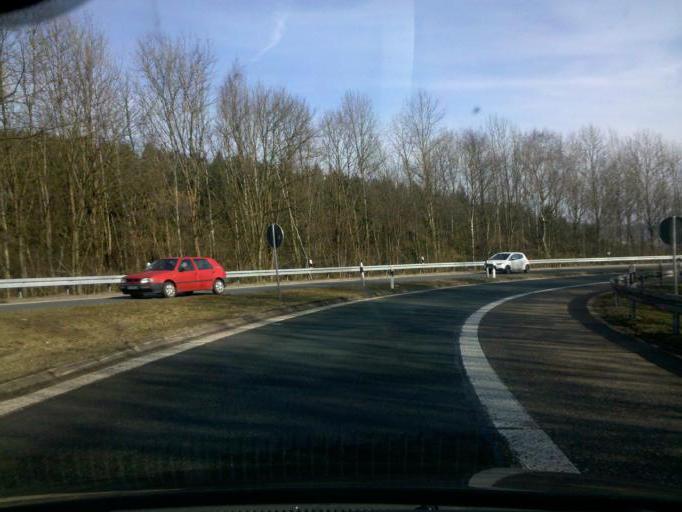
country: DE
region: North Rhine-Westphalia
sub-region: Regierungsbezirk Arnsberg
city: Drolshagen
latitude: 51.0574
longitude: 7.7649
